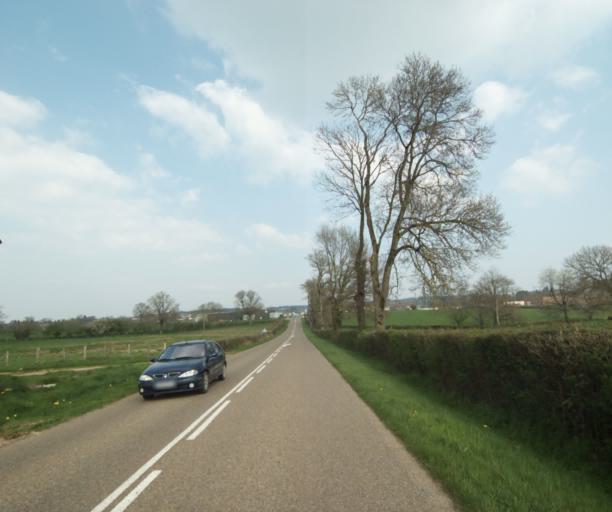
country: FR
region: Bourgogne
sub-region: Departement de Saone-et-Loire
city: Charolles
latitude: 46.4793
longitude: 4.4262
